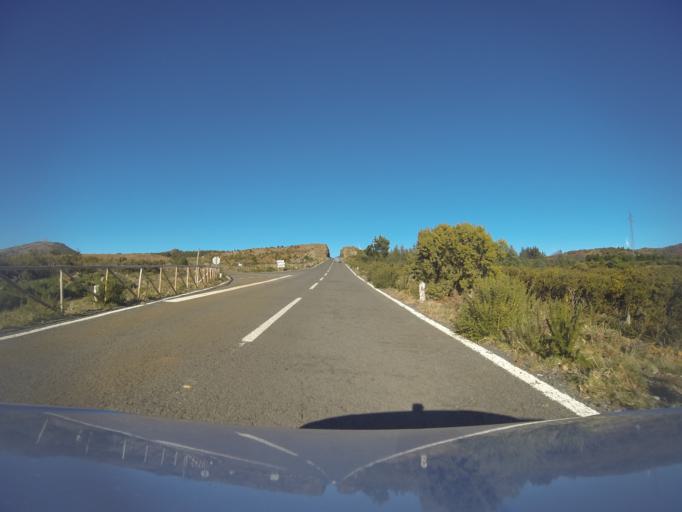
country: PT
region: Madeira
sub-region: Sao Vicente
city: Sao Vicente
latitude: 32.7668
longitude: -17.0806
